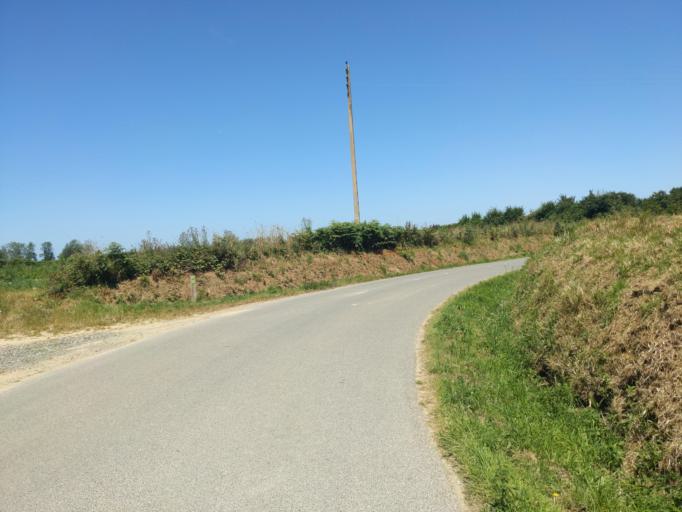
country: FR
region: Brittany
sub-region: Departement des Cotes-d'Armor
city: Plougrescant
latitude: 48.8167
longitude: -3.2138
